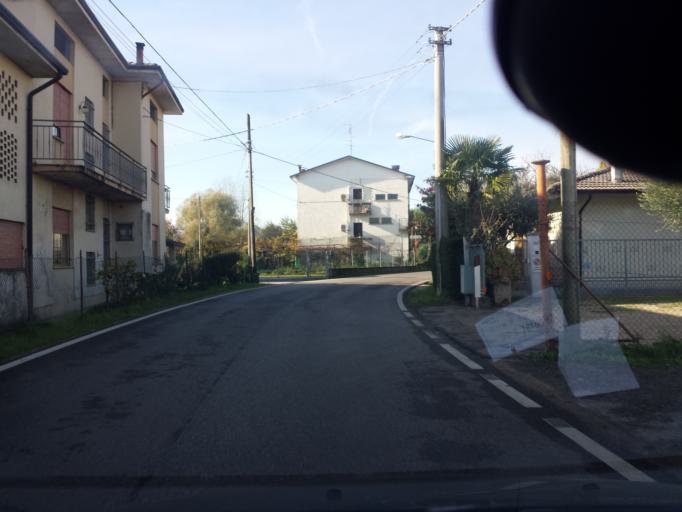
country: IT
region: Veneto
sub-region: Provincia di Vicenza
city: Caldogno-Rettorgole-Cresole
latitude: 45.6103
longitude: 11.5209
